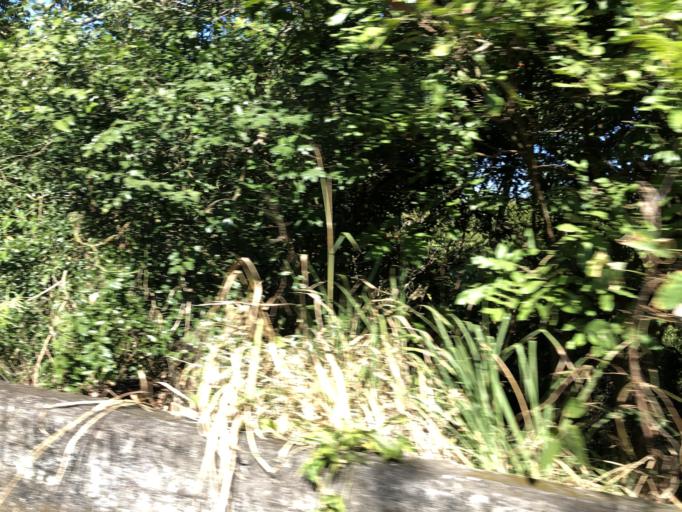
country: TW
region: Taiwan
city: Yujing
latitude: 23.0258
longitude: 120.3868
